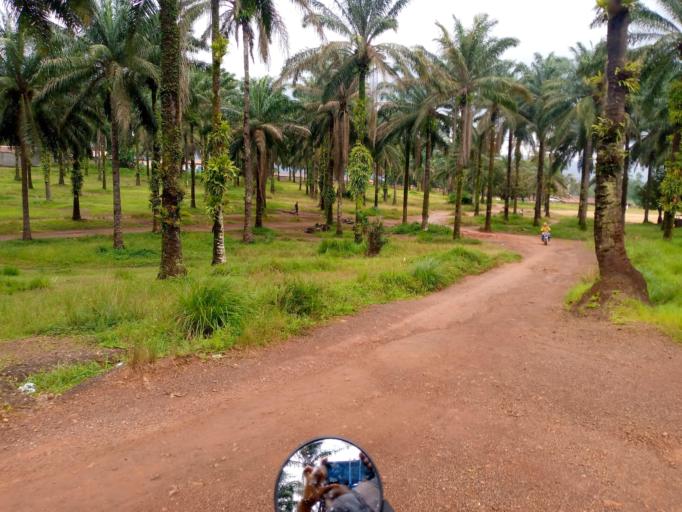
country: SL
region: Eastern Province
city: Kenema
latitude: 7.8640
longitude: -11.1848
